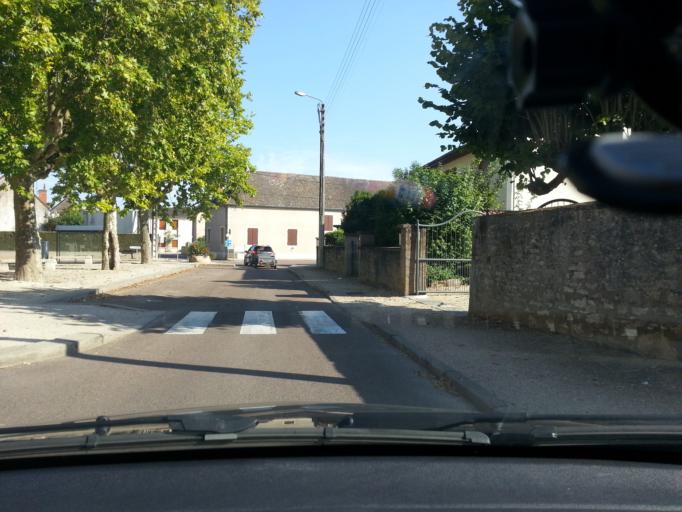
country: FR
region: Bourgogne
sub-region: Departement de Saone-et-Loire
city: Saint-Remy
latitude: 46.7665
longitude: 4.8176
